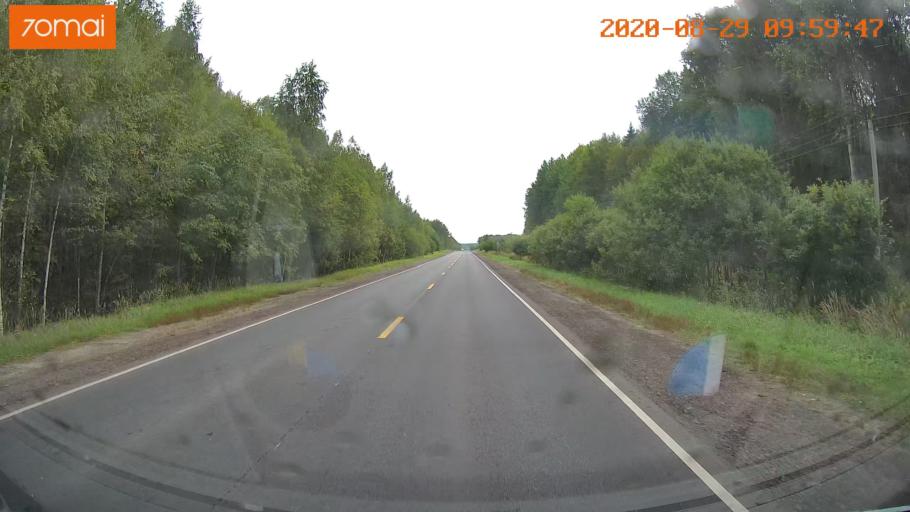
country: RU
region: Ivanovo
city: Zarechnyy
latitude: 57.4106
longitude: 42.3753
